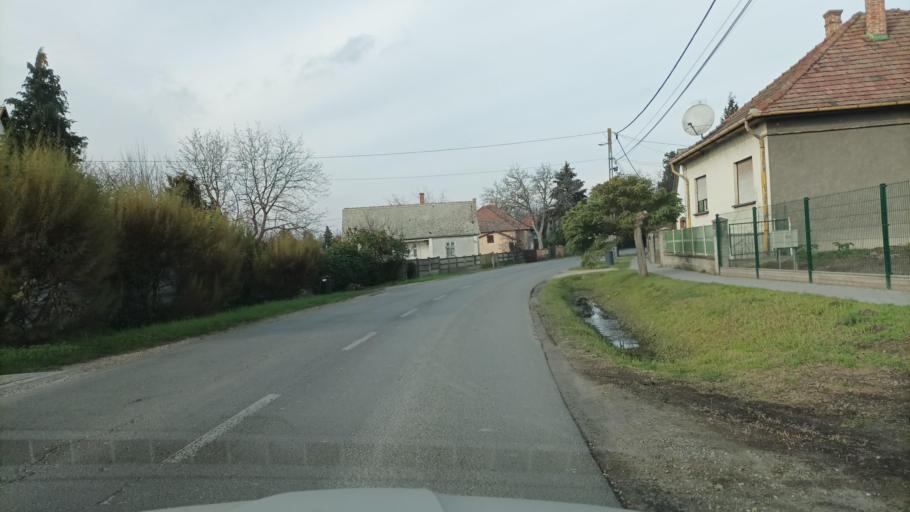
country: HU
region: Pest
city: Rackeve
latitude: 47.1305
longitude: 18.9484
